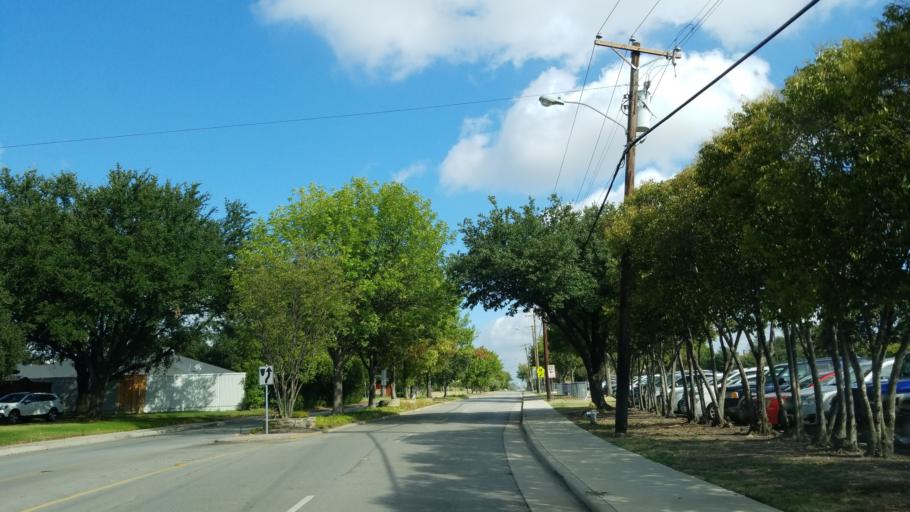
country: US
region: Texas
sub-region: Dallas County
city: Richardson
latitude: 32.9466
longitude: -96.7786
